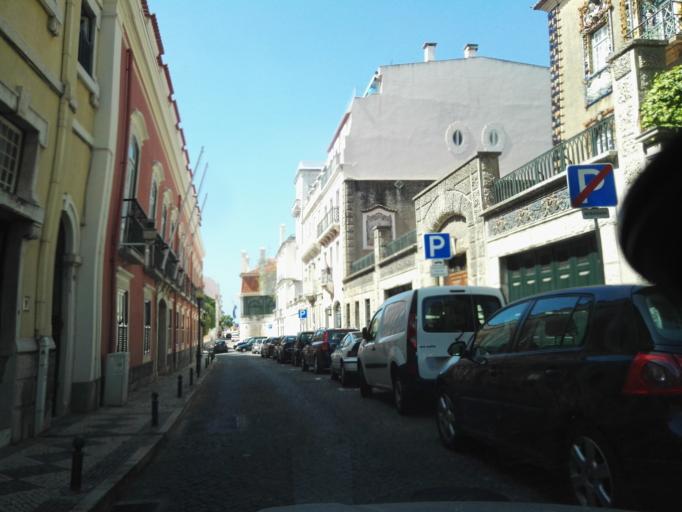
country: PT
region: Setubal
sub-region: Almada
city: Cacilhas
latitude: 38.7084
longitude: -9.1628
